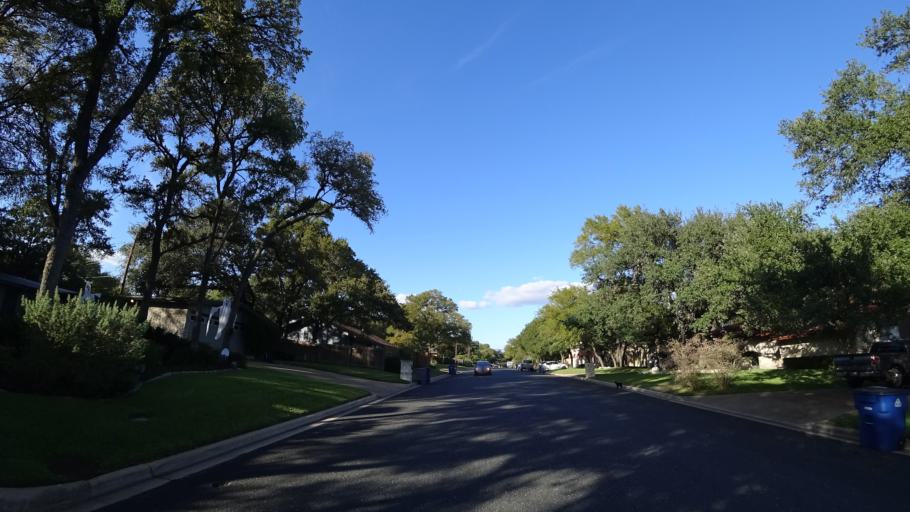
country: US
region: Texas
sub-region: Williamson County
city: Jollyville
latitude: 30.3653
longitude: -97.7471
